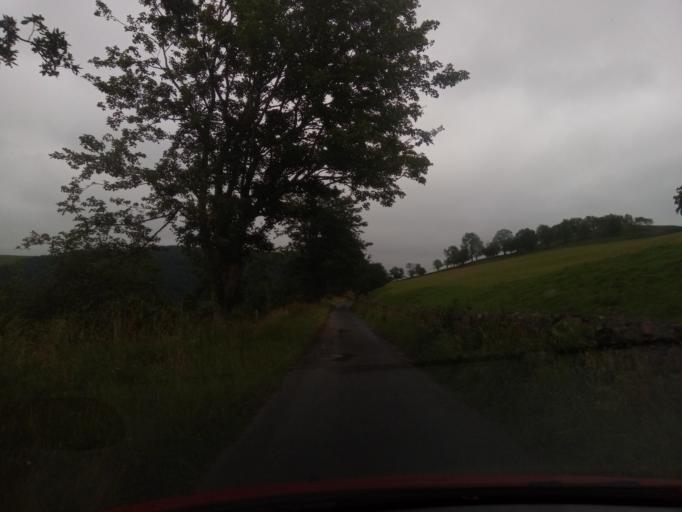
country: GB
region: Scotland
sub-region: Fife
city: Pathhead
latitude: 55.7554
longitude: -2.9277
